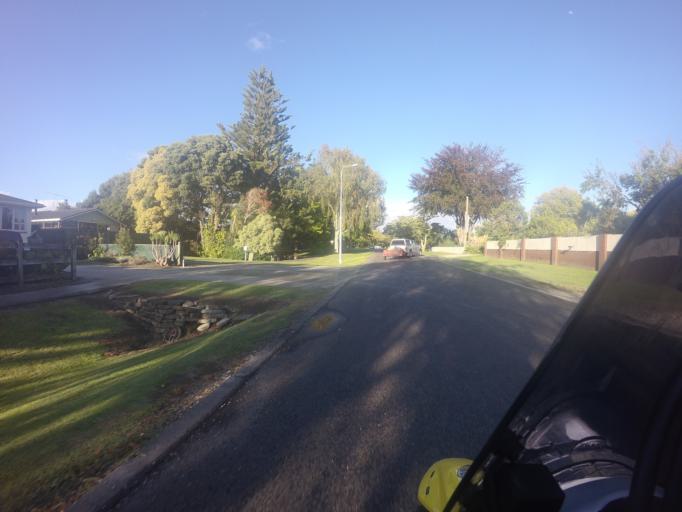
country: NZ
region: Gisborne
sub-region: Gisborne District
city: Gisborne
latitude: -38.6666
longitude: 178.0451
